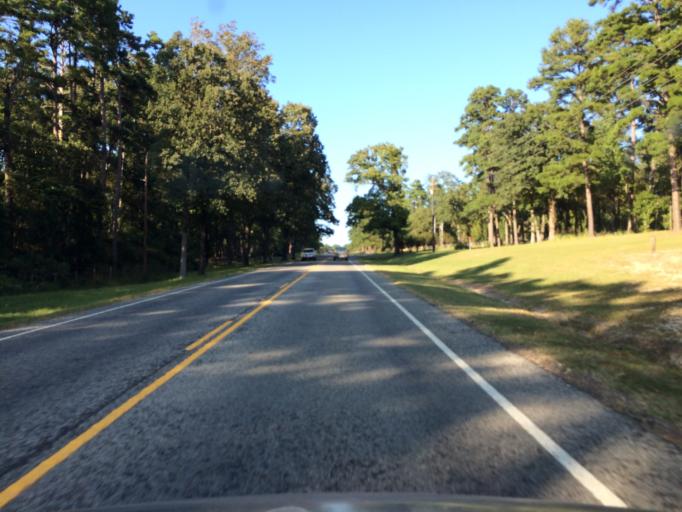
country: US
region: Texas
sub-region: Wood County
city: Hawkins
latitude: 32.7143
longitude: -95.2013
